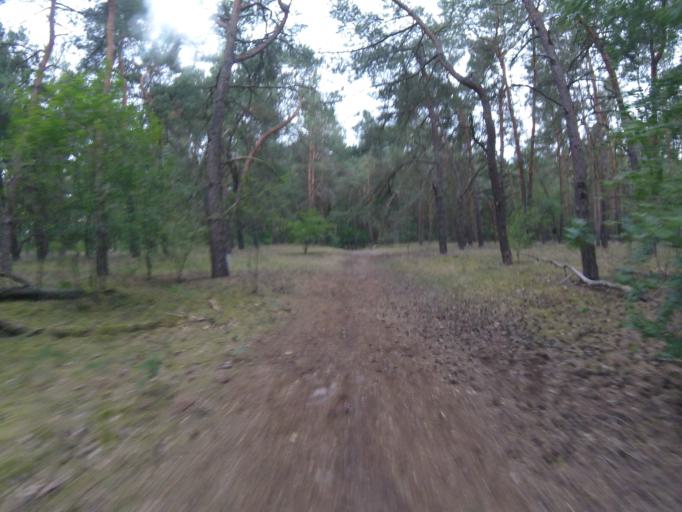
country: DE
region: Brandenburg
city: Bestensee
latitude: 52.2146
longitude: 13.6210
